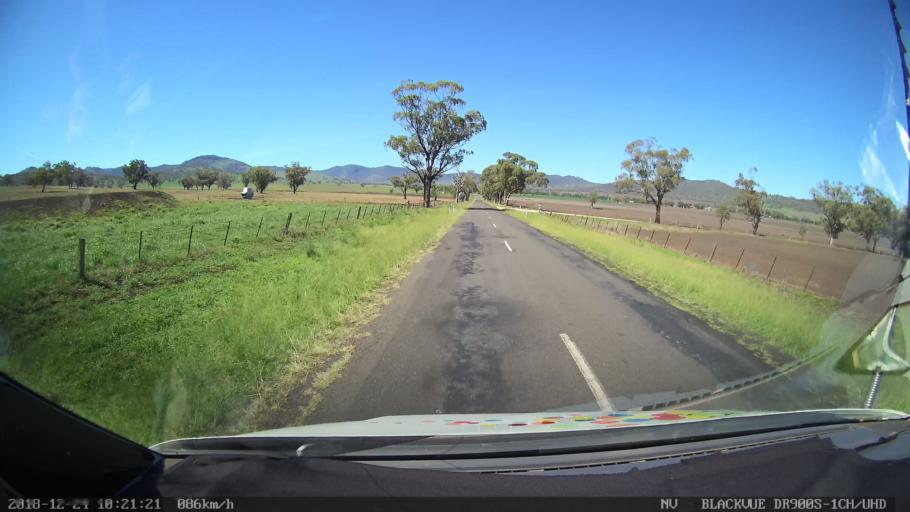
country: AU
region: New South Wales
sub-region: Liverpool Plains
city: Quirindi
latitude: -31.7513
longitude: 150.5513
